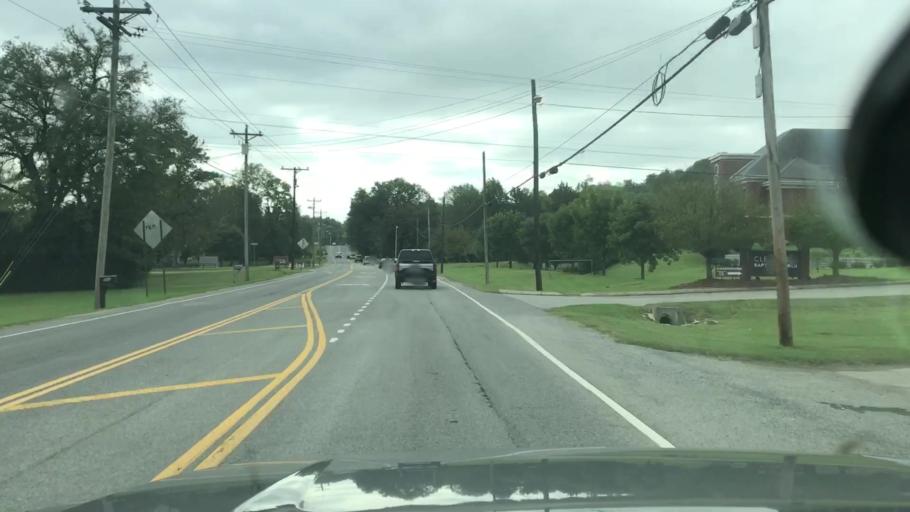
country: US
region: Tennessee
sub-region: Williamson County
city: Franklin
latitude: 35.9676
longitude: -86.8377
